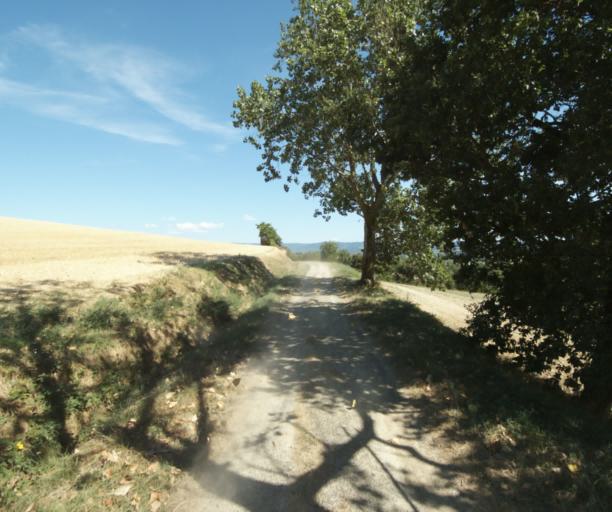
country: FR
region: Midi-Pyrenees
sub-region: Departement de la Haute-Garonne
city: Saint-Felix-Lauragais
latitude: 43.4984
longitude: 1.9335
